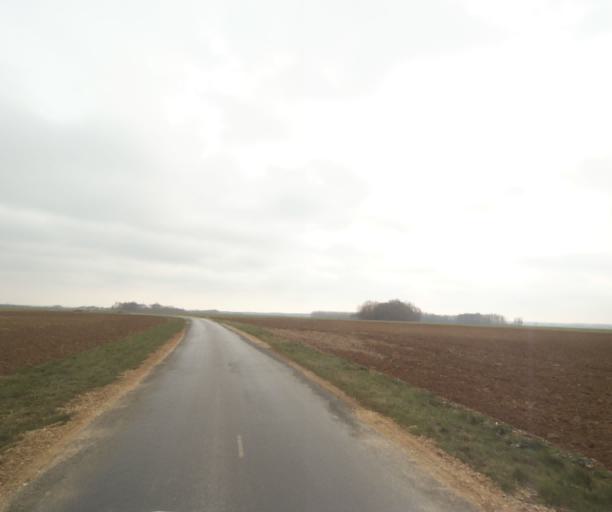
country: FR
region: Champagne-Ardenne
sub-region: Departement de la Marne
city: Pargny-sur-Saulx
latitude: 48.6895
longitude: 4.8087
